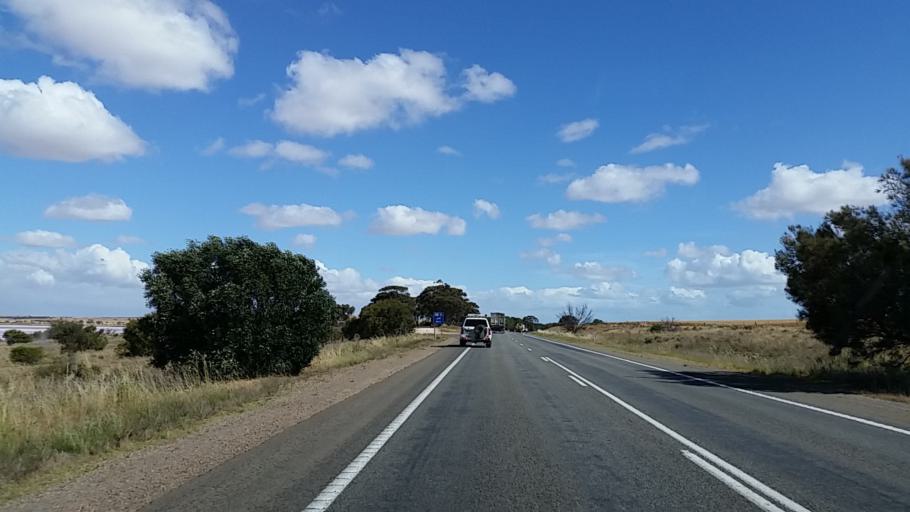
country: AU
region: South Australia
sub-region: Wakefield
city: Balaklava
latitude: -33.9117
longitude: 138.1628
